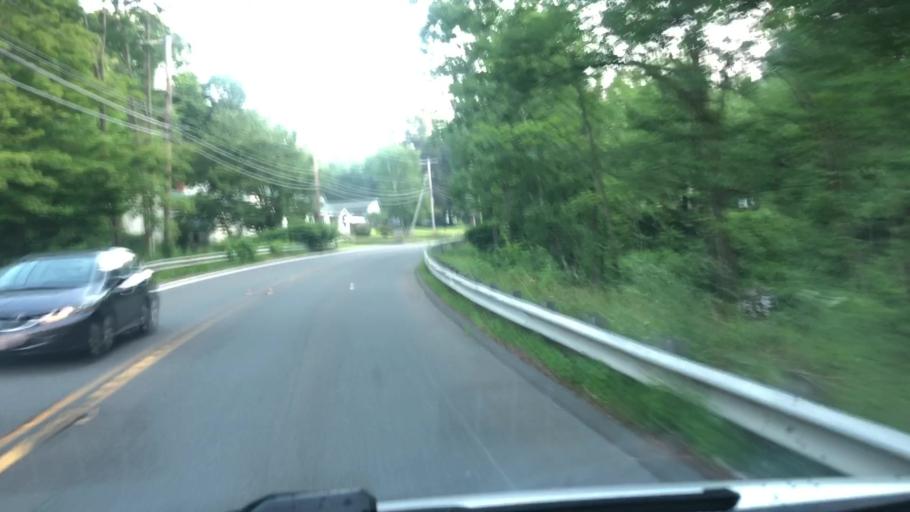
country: US
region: Massachusetts
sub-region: Hampshire County
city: Williamsburg
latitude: 42.4007
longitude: -72.7448
